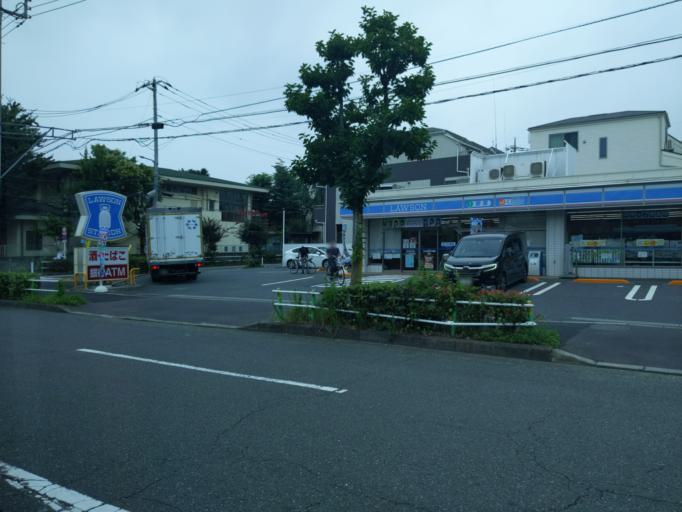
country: JP
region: Saitama
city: Wako
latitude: 35.7890
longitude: 139.6525
